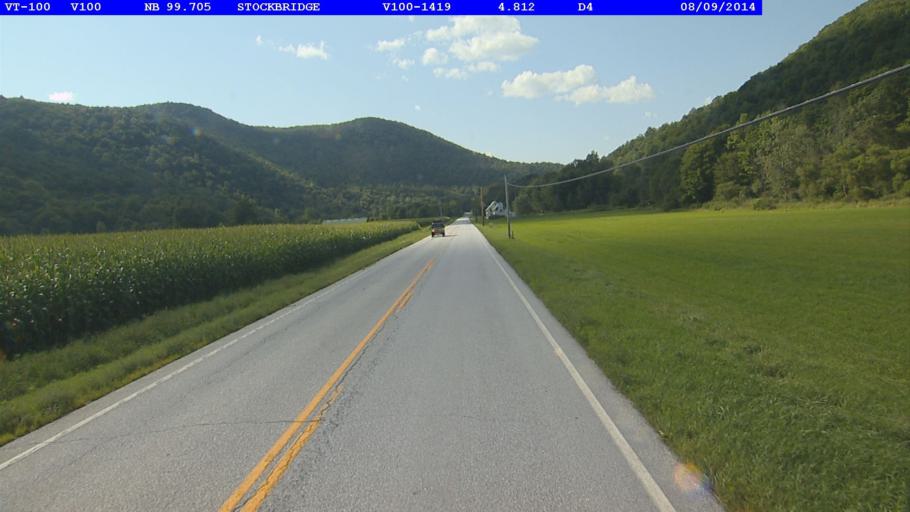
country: US
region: Vermont
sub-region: Orange County
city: Randolph
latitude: 43.8030
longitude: -72.7776
